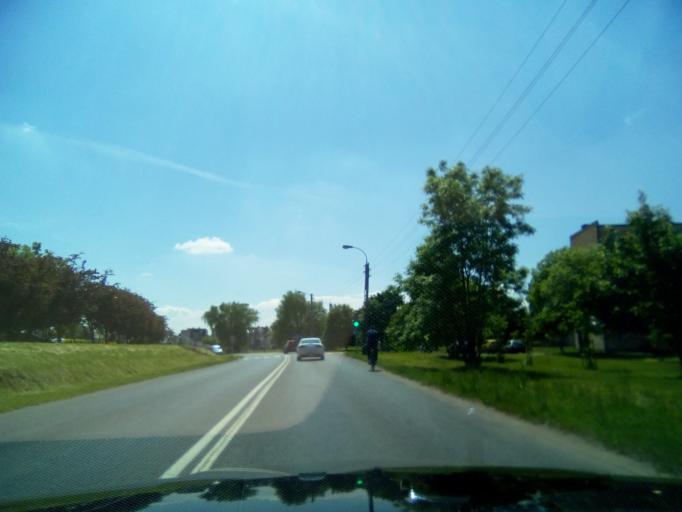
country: PL
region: Greater Poland Voivodeship
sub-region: Powiat gnieznienski
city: Gniezno
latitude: 52.5508
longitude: 17.6038
